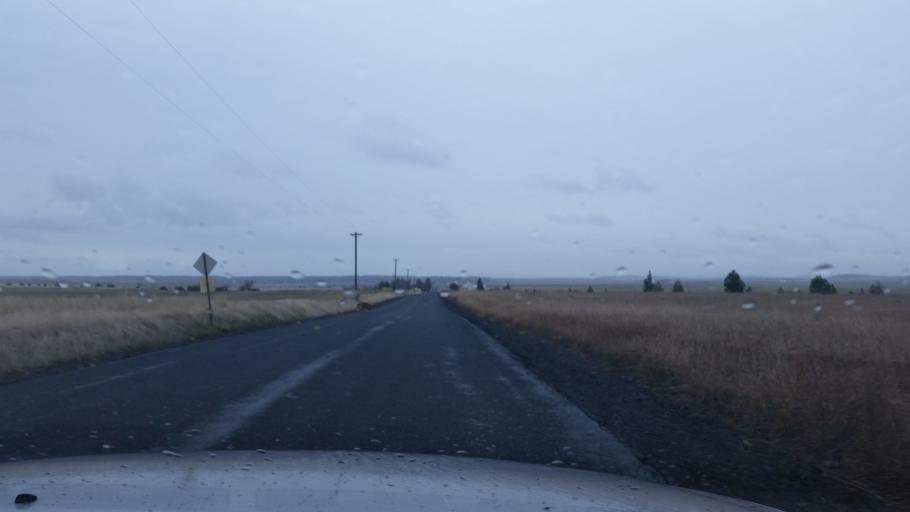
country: US
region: Washington
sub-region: Spokane County
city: Medical Lake
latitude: 47.6146
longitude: -117.7967
